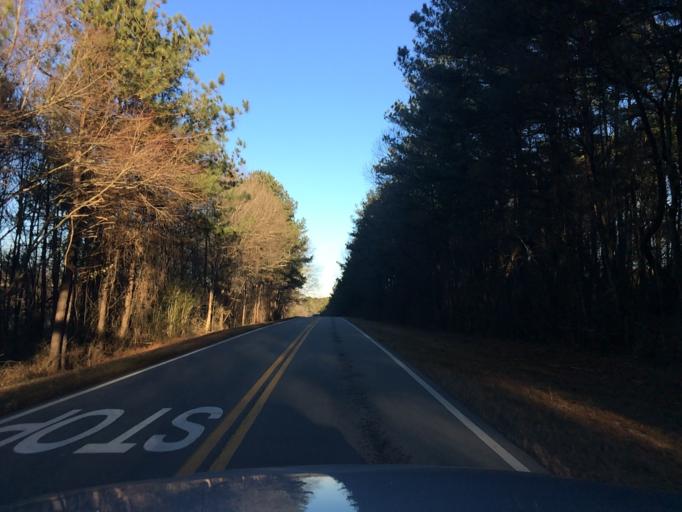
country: US
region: Georgia
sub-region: Barrow County
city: Winder
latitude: 33.9703
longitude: -83.7783
